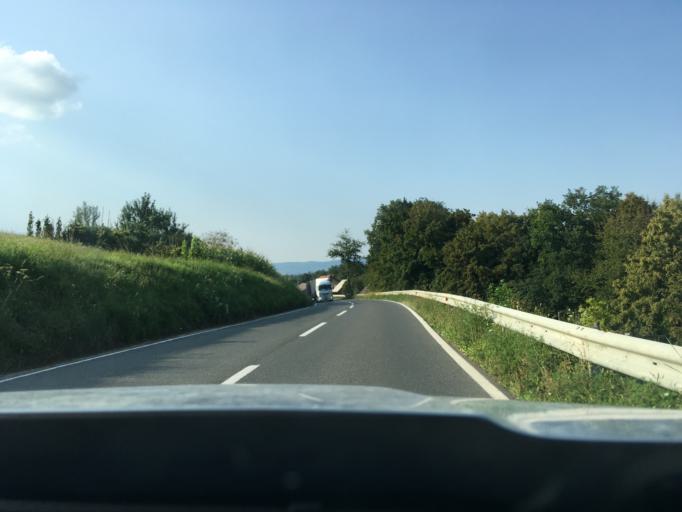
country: SI
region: Novo Mesto
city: Novo Mesto
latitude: 45.7710
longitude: 15.1911
